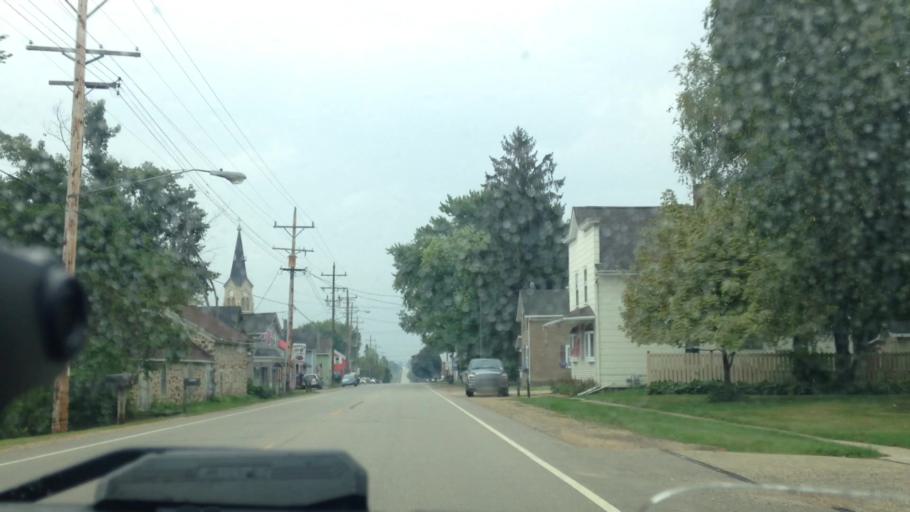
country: US
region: Wisconsin
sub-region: Washington County
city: Slinger
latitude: 43.3711
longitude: -88.3347
